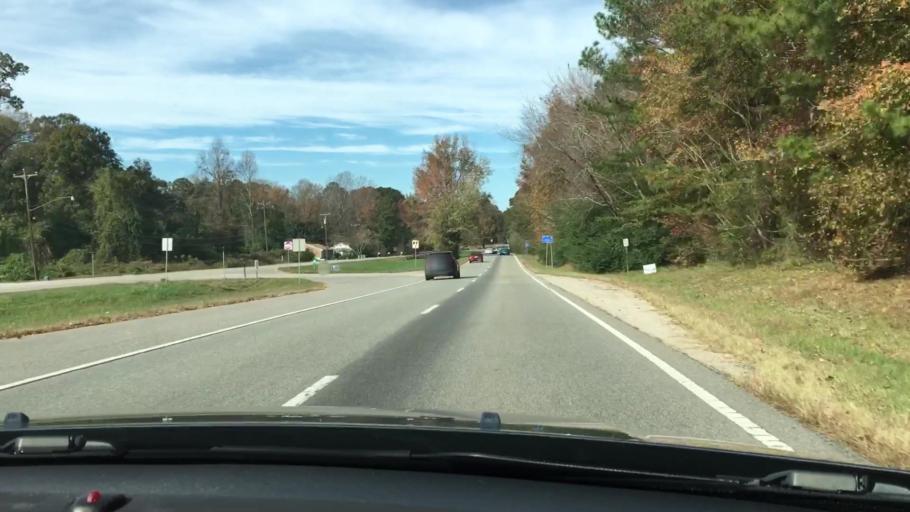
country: US
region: Virginia
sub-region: James City County
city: Williamsburg
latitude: 37.3286
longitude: -76.7415
